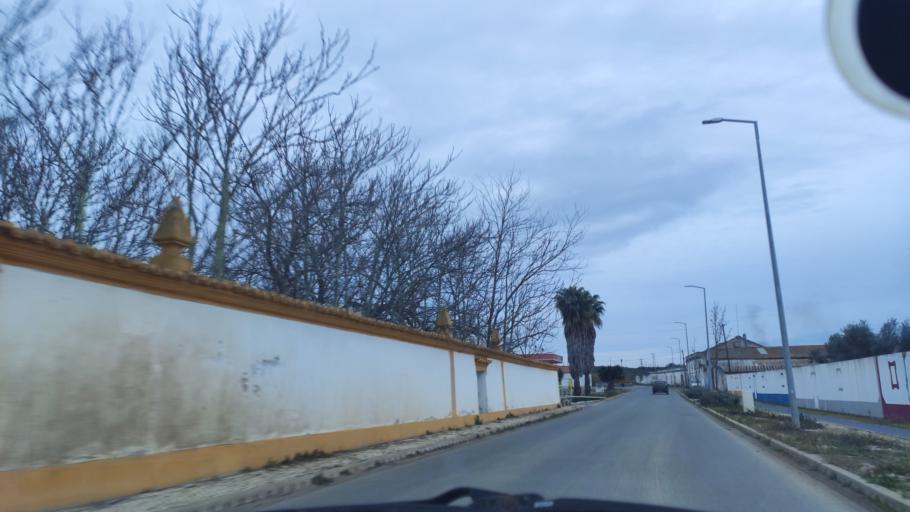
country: PT
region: Beja
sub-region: Beja
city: Ferreira do Alentejo
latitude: 38.0590
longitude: -8.1098
